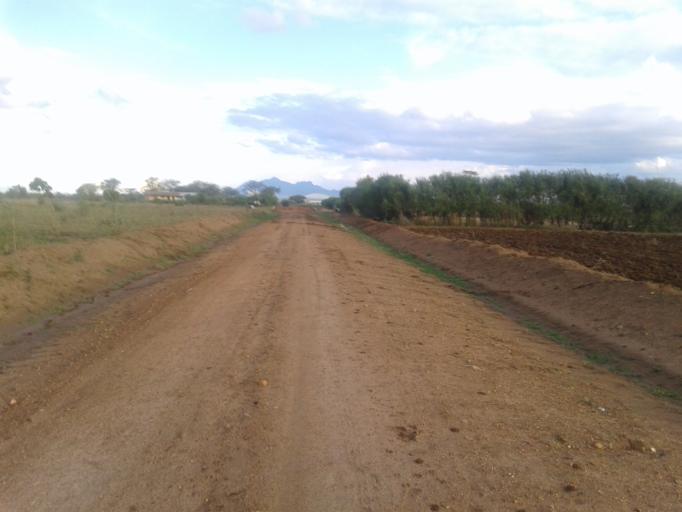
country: UG
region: Northern Region
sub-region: Kotido District
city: Kotido
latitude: 2.9965
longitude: 34.1045
